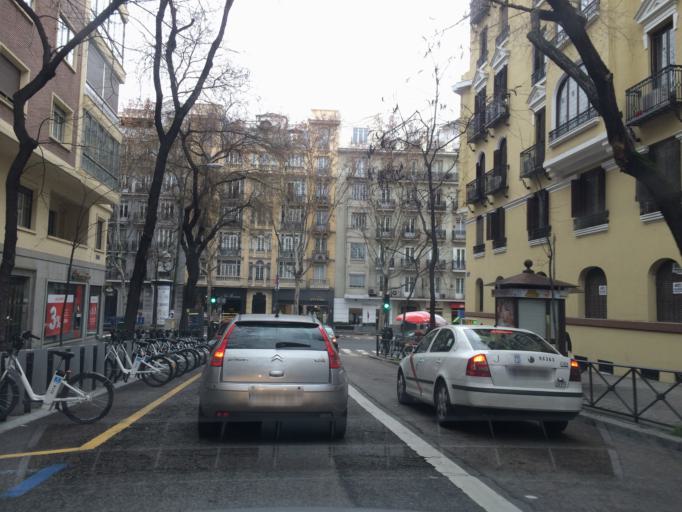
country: ES
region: Madrid
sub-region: Provincia de Madrid
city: Chamberi
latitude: 40.4308
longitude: -3.7135
